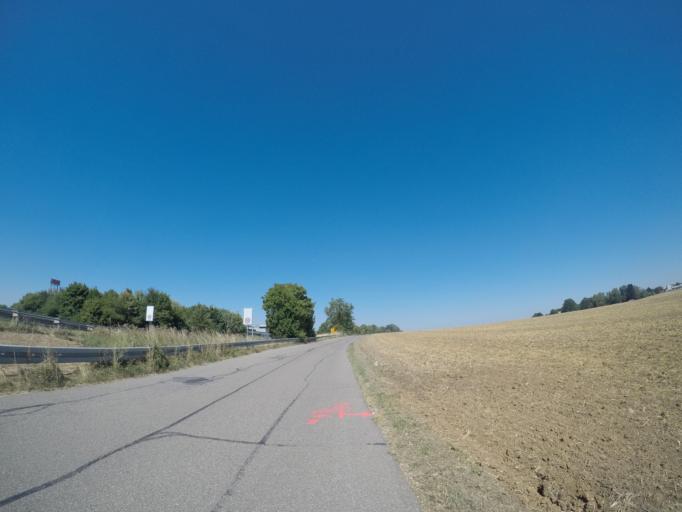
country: DE
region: Baden-Wuerttemberg
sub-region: Tuebingen Region
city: Dornstadt
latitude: 48.4592
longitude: 9.9571
